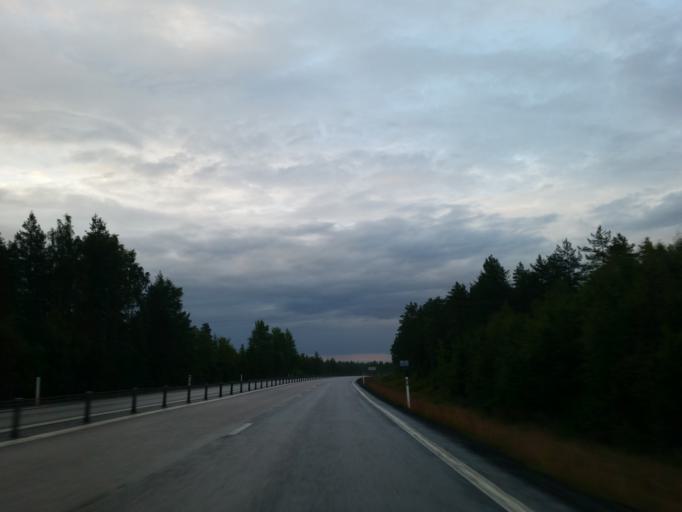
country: SE
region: Vaesterbotten
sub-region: Umea Kommun
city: Saevar
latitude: 63.9513
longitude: 20.6650
